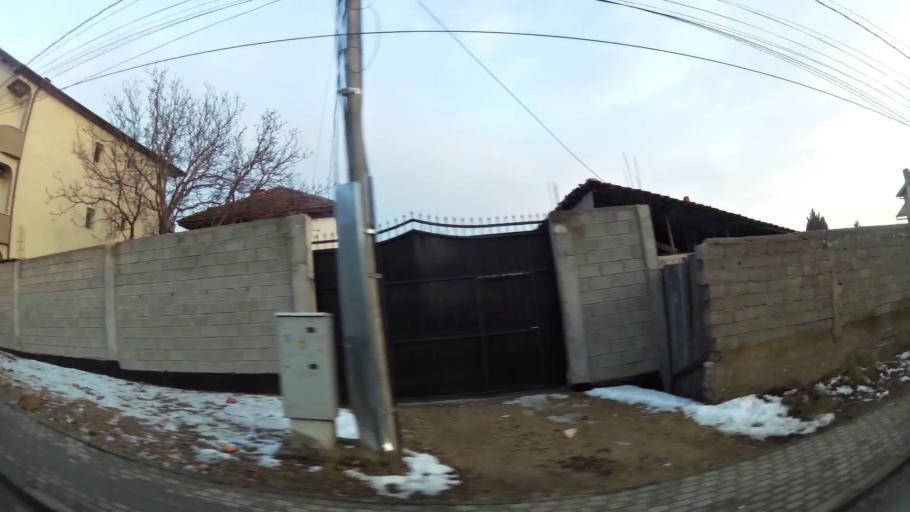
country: MK
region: Aracinovo
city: Arachinovo
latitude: 42.0287
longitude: 21.5646
